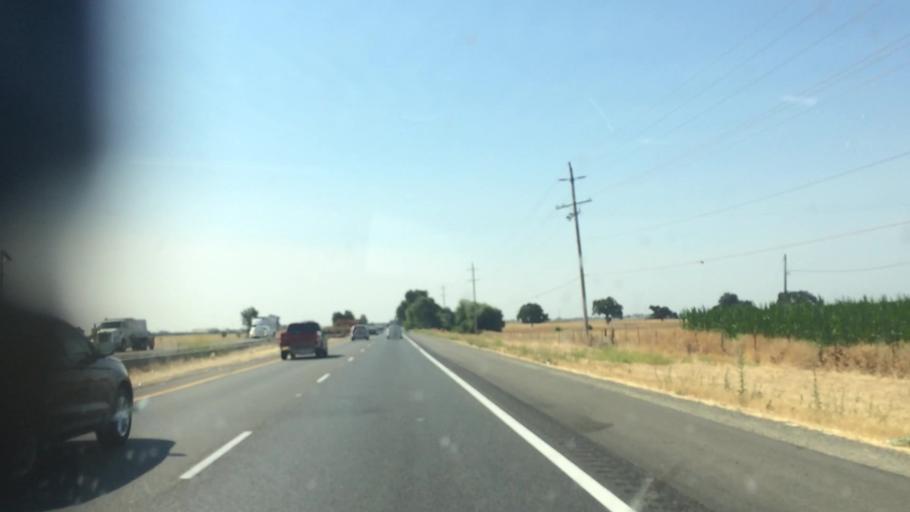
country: US
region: California
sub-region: Sacramento County
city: Elk Grove
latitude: 38.3345
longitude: -121.3317
